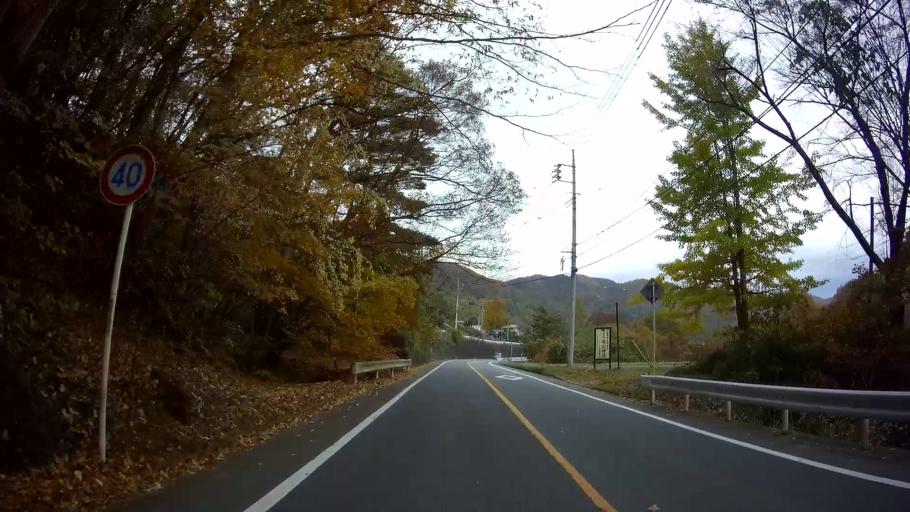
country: JP
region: Gunma
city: Nakanojomachi
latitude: 36.5685
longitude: 138.6320
